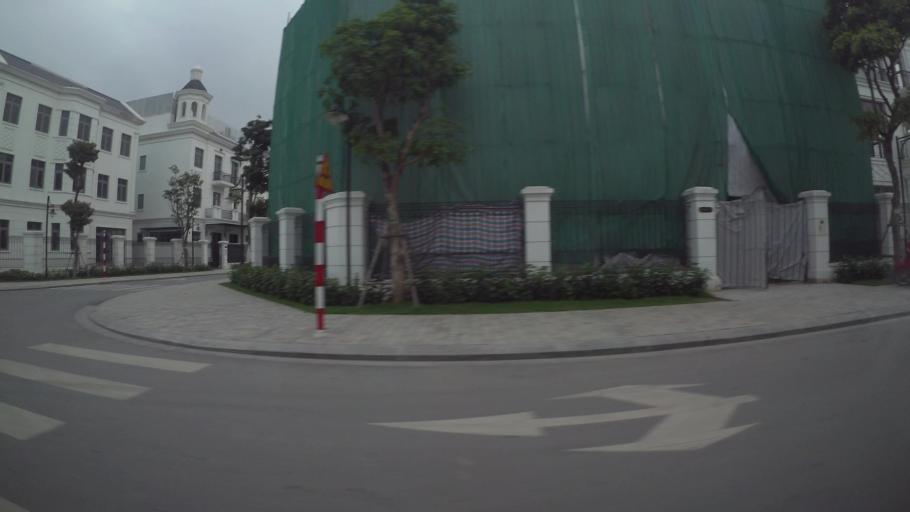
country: VN
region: Ha Noi
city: Trau Quy
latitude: 21.0503
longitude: 105.9034
